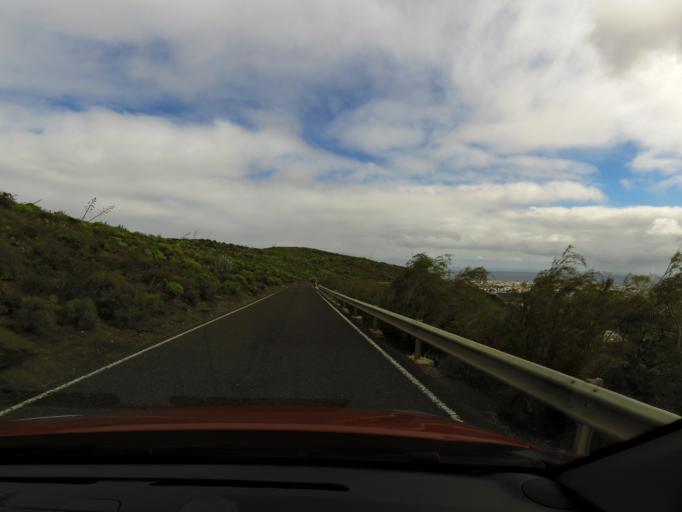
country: ES
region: Canary Islands
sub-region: Provincia de Las Palmas
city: Telde
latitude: 28.0143
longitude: -15.4443
